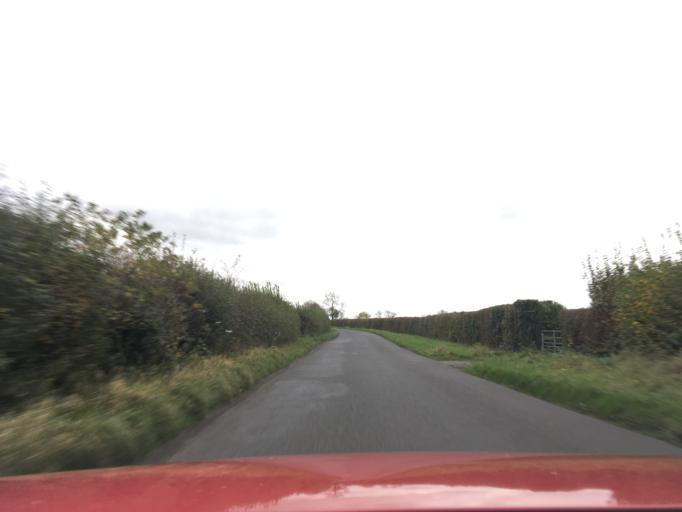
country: GB
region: England
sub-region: Somerset
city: Yeovil
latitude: 51.0138
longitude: -2.5995
